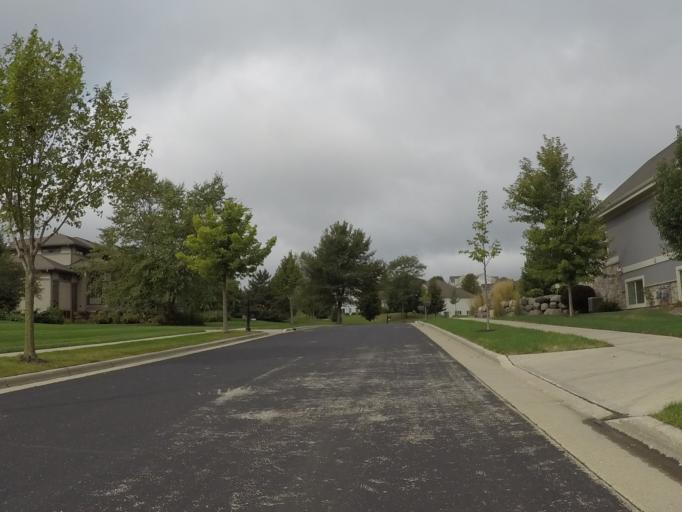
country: US
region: Wisconsin
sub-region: Dane County
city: Verona
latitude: 43.0408
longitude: -89.5412
